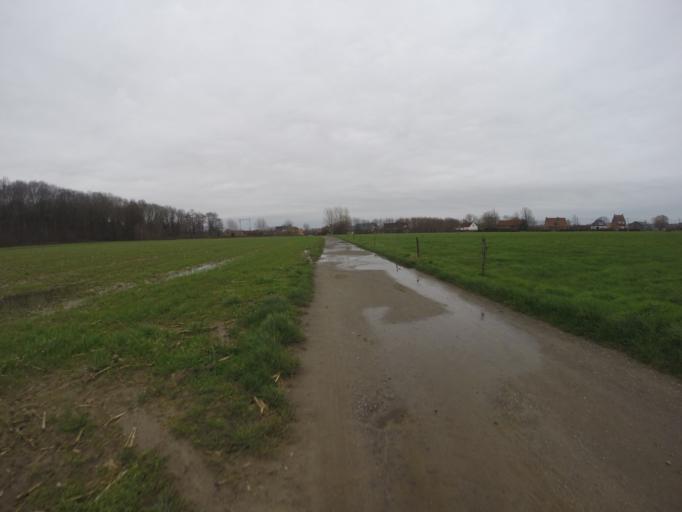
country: BE
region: Flanders
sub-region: Provincie Oost-Vlaanderen
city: Aalter
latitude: 51.1253
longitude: 3.4683
